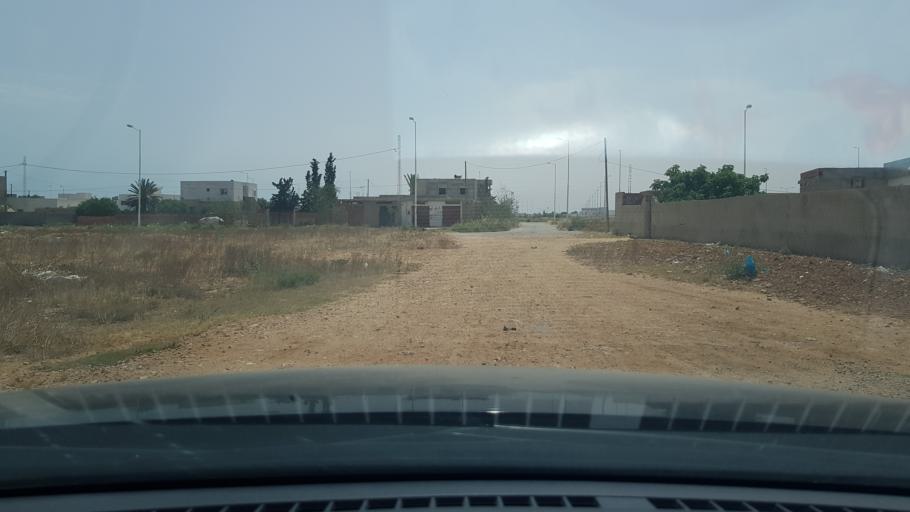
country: TN
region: Safaqis
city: Al Qarmadah
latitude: 34.8301
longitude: 10.7502
